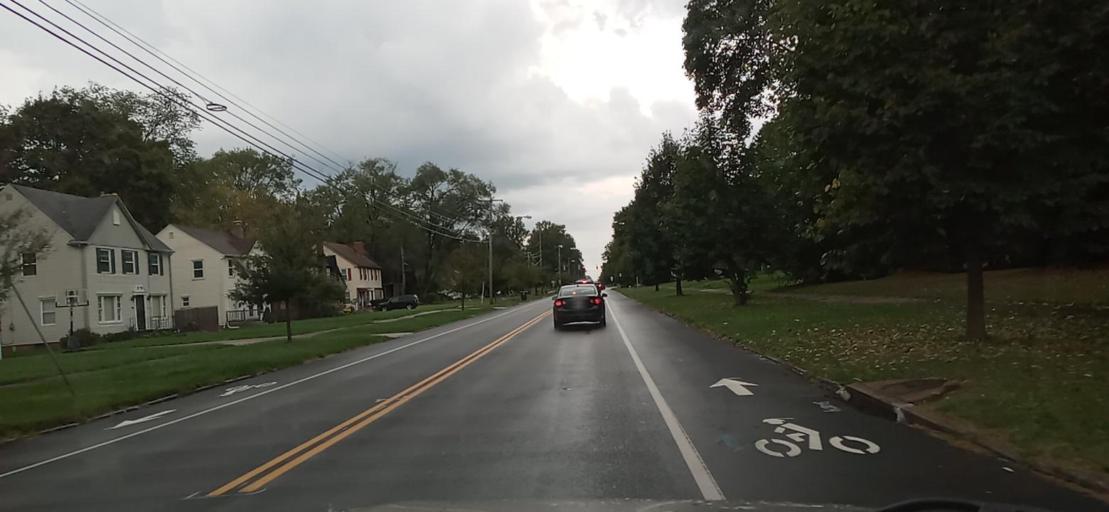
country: US
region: Ohio
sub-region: Summit County
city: Akron
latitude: 41.0906
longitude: -81.5694
